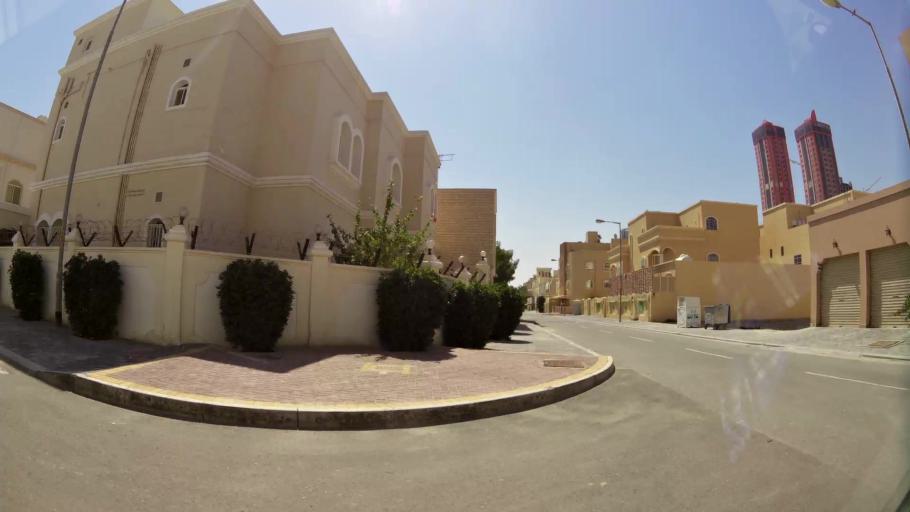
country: BH
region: Manama
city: Manama
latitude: 26.2186
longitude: 50.6136
